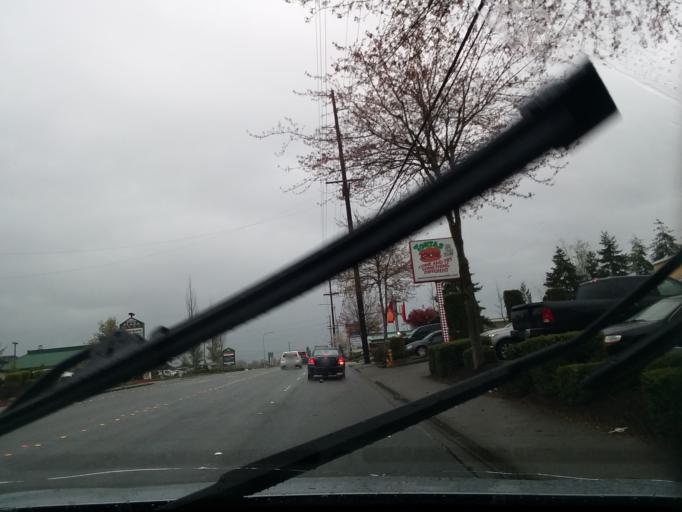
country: US
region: Washington
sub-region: King County
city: Fairwood
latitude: 47.4886
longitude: -122.1674
